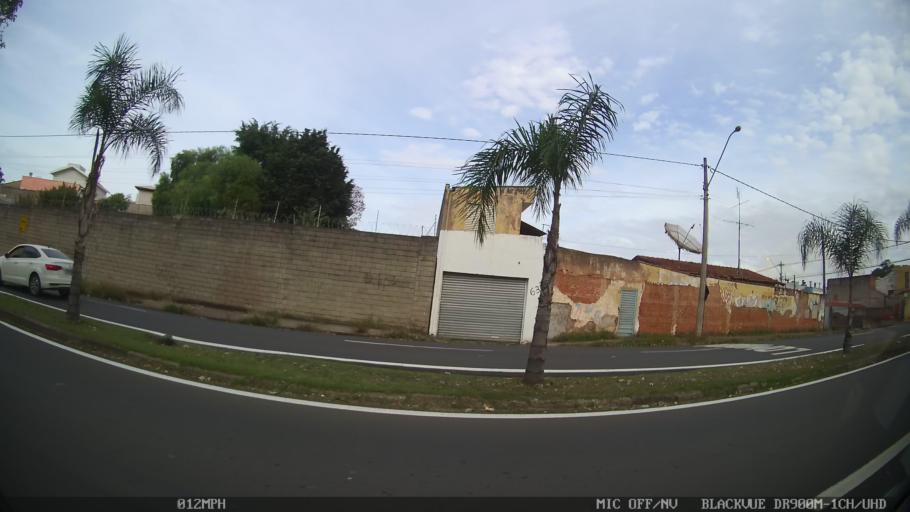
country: BR
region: Sao Paulo
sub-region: Piracicaba
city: Piracicaba
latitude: -22.7454
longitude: -47.6320
